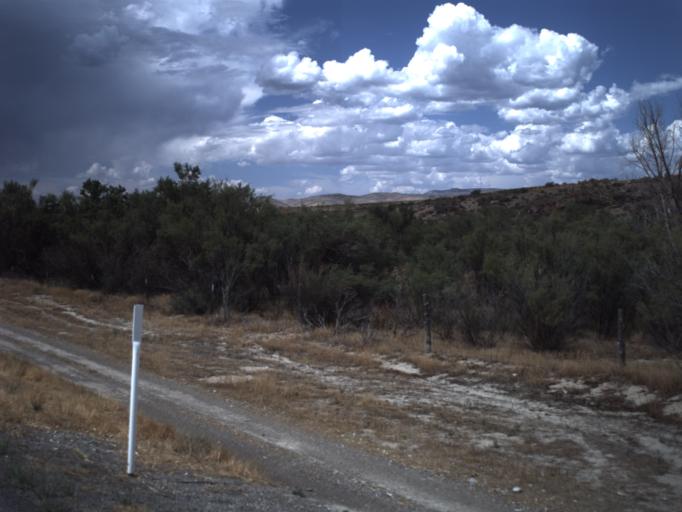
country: US
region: Utah
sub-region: Sanpete County
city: Centerfield
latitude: 39.1381
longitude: -111.7828
